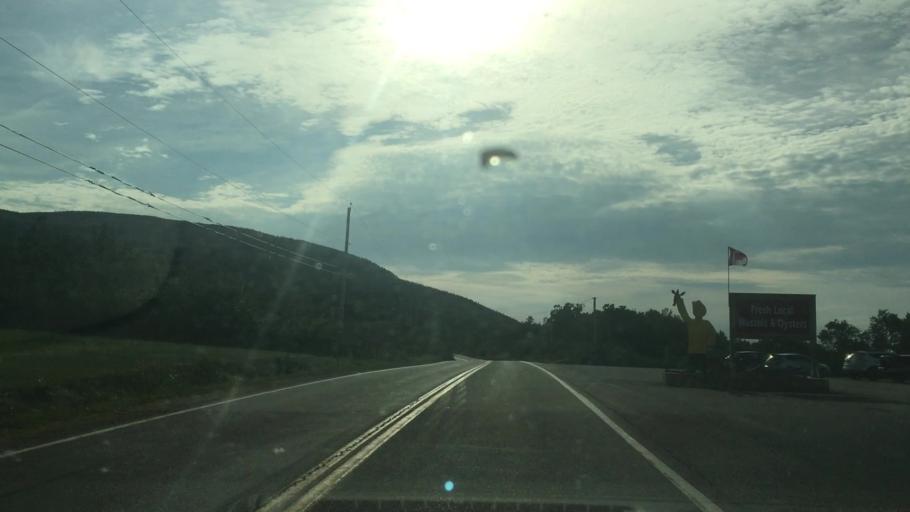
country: CA
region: Nova Scotia
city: Sydney Mines
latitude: 46.8242
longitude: -60.8195
